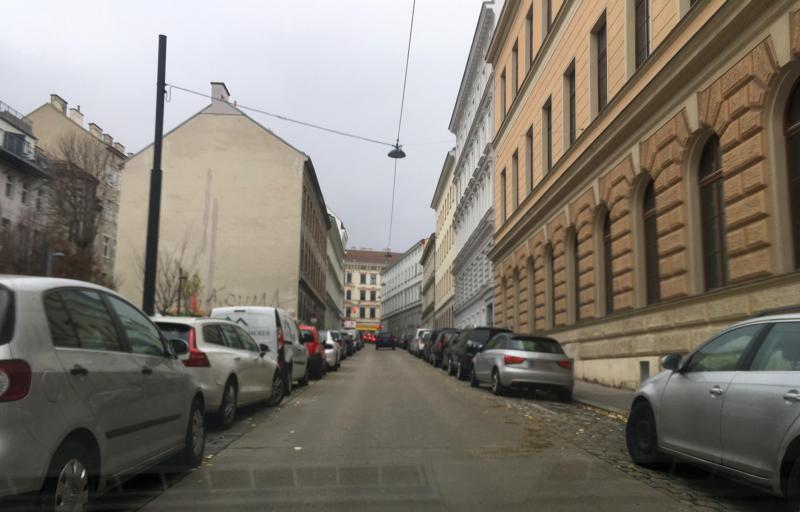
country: AT
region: Vienna
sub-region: Wien Stadt
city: Vienna
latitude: 48.1905
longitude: 16.3319
